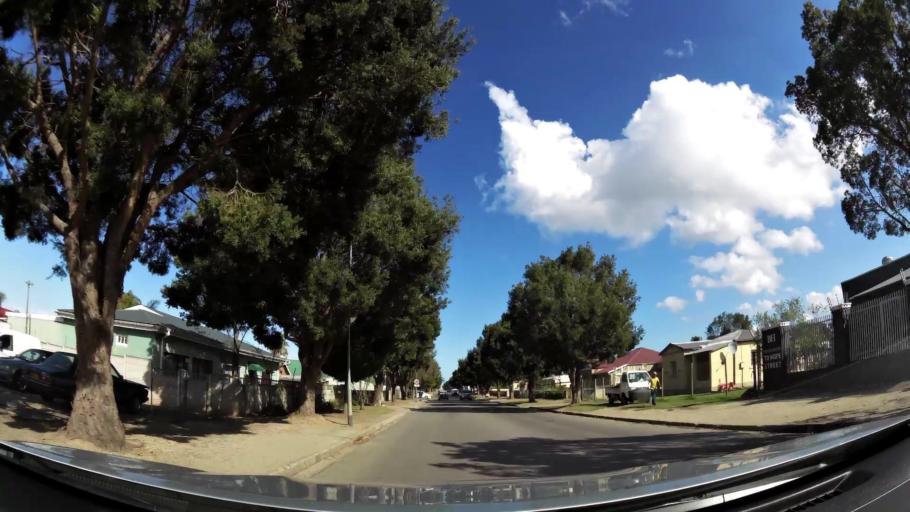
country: ZA
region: Western Cape
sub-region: Eden District Municipality
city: George
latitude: -33.9699
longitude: 22.4632
